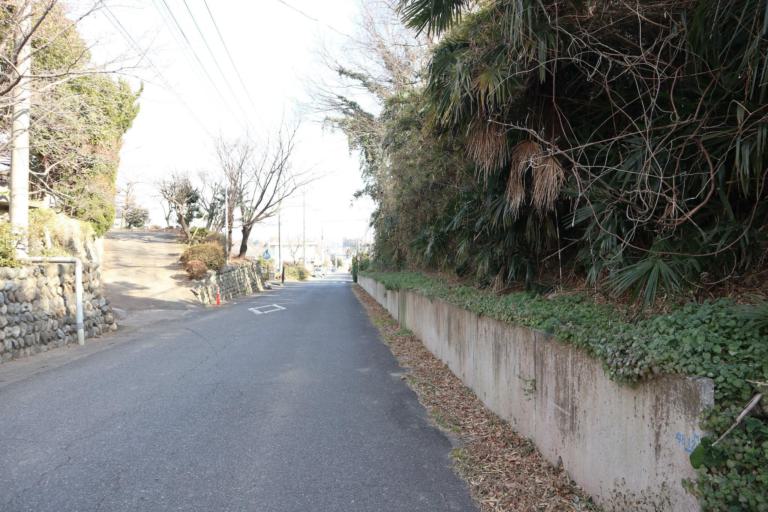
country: JP
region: Saitama
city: Fukiage-fujimi
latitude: 36.0735
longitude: 139.4265
